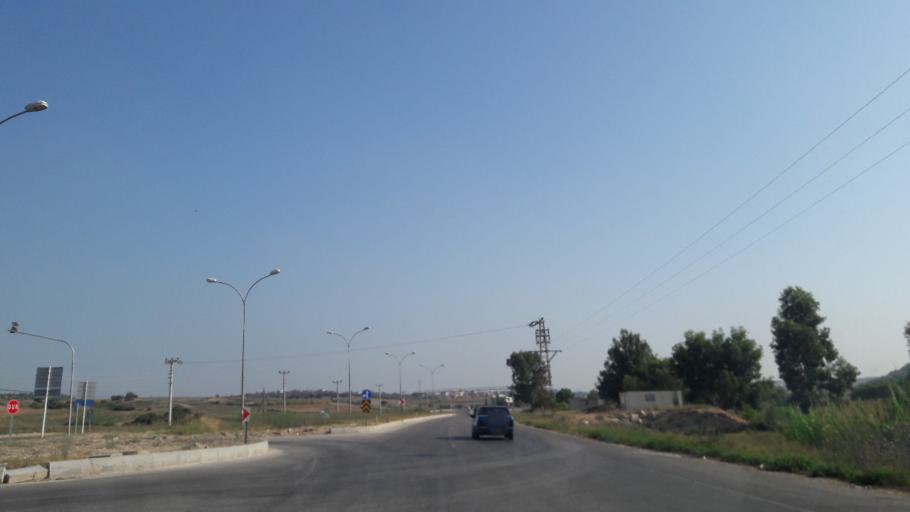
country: TR
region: Adana
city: Yuregir
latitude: 37.0616
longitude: 35.4446
